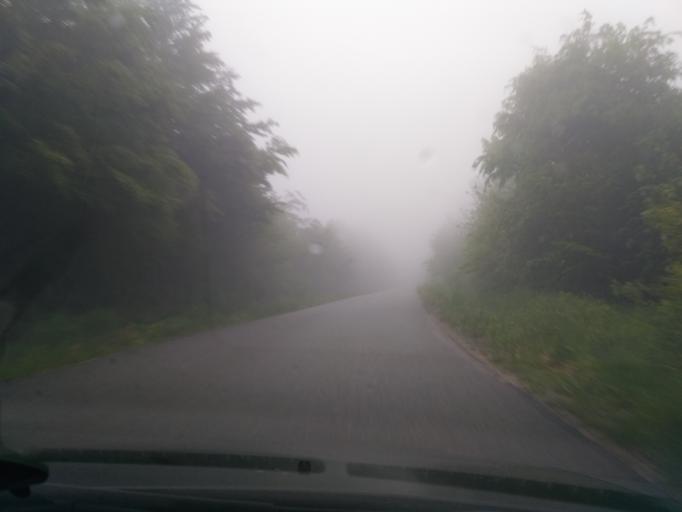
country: PL
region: Subcarpathian Voivodeship
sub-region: Powiat debicki
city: Debica
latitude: 49.9765
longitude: 21.4061
